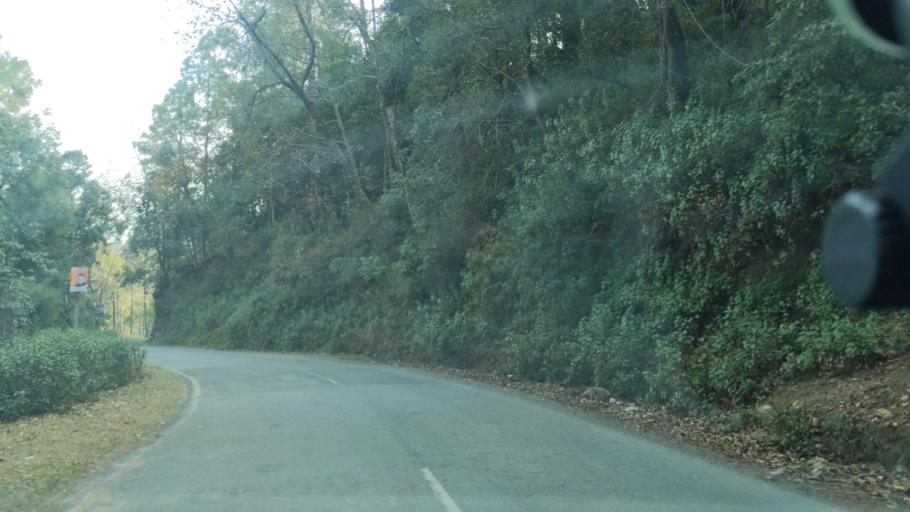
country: IN
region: Uttarakhand
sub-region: Naini Tal
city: Bhowali
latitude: 29.4050
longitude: 79.5386
